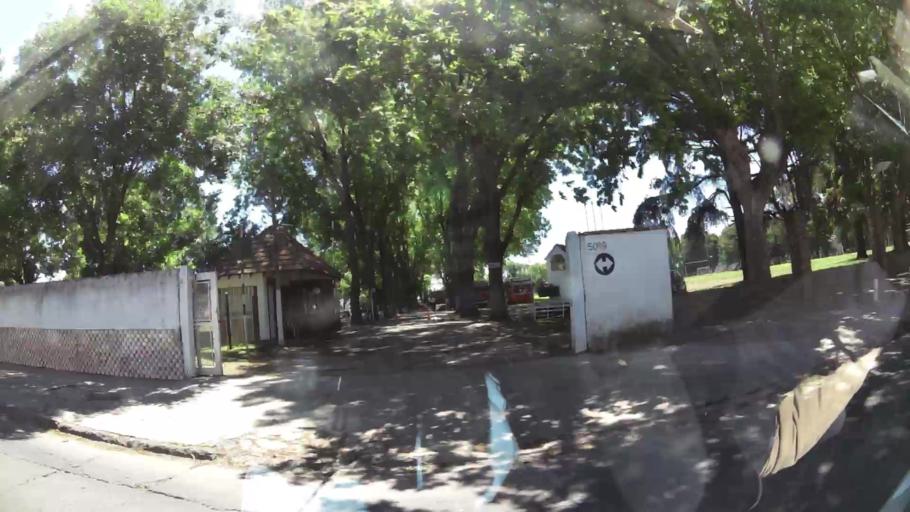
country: AR
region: Buenos Aires
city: Caseros
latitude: -34.5786
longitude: -58.5575
